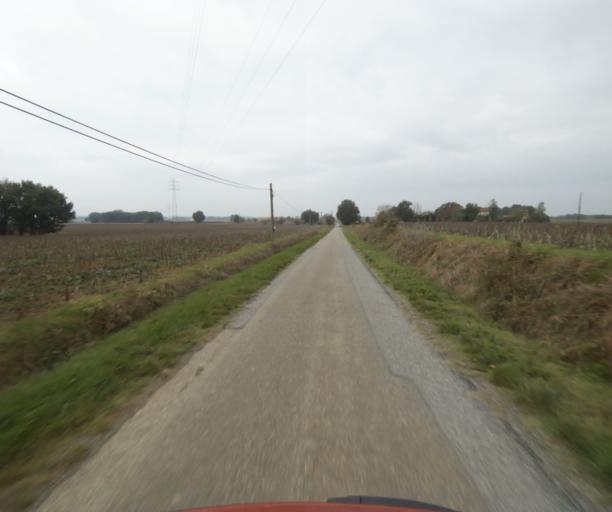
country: FR
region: Midi-Pyrenees
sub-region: Departement du Tarn-et-Garonne
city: Verdun-sur-Garonne
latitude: 43.8417
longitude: 1.1836
